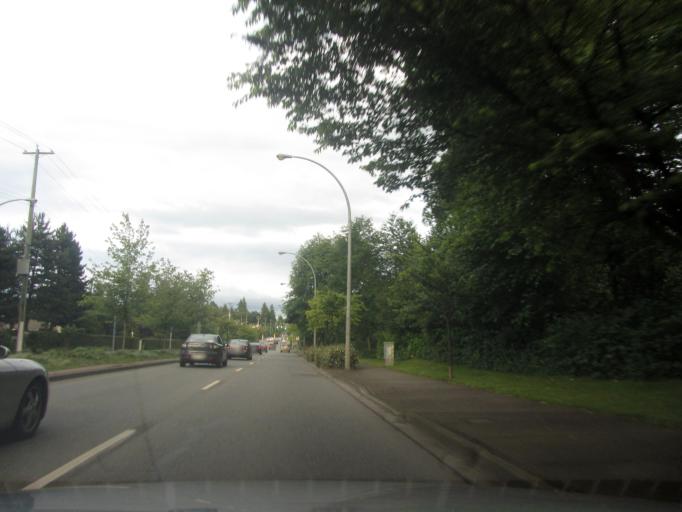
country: CA
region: British Columbia
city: Walnut Grove
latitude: 49.1627
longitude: -122.6495
